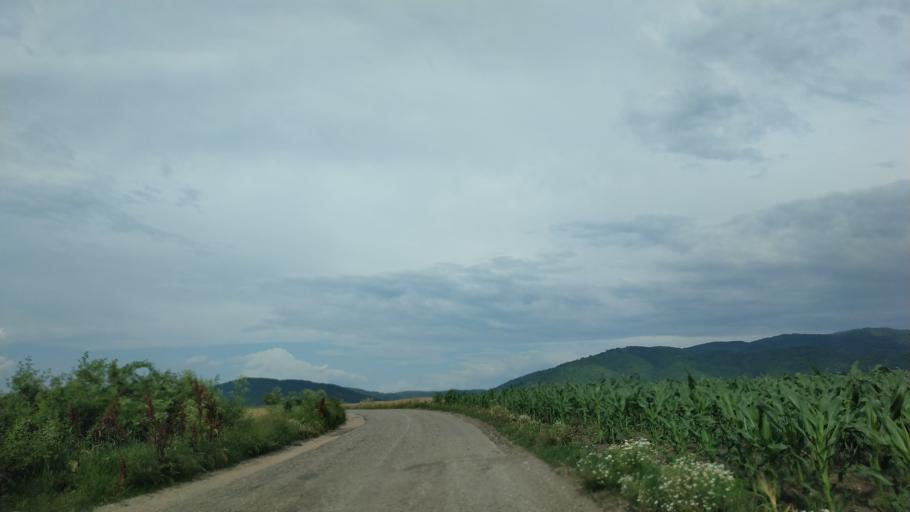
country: RS
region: Central Serbia
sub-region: Nisavski Okrug
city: Aleksinac
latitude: 43.6158
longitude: 21.6714
